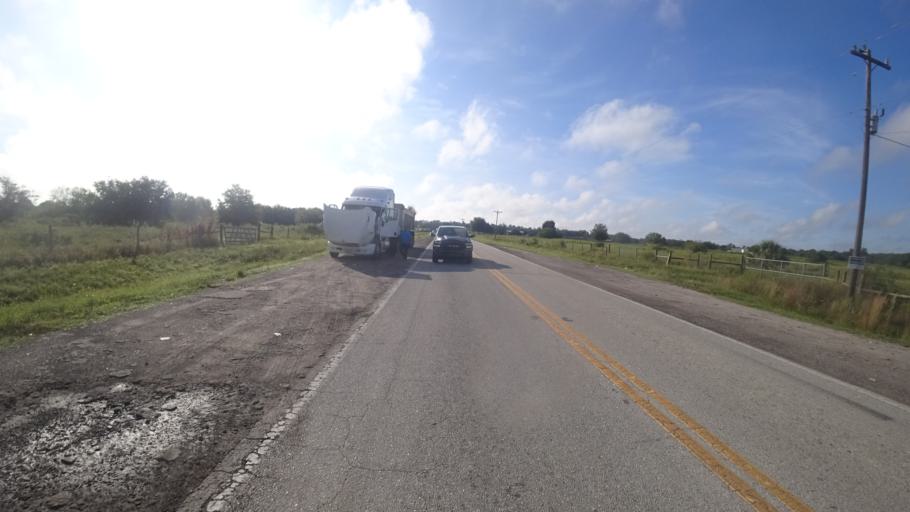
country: US
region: Florida
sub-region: Sarasota County
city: The Meadows
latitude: 27.4741
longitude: -82.3067
